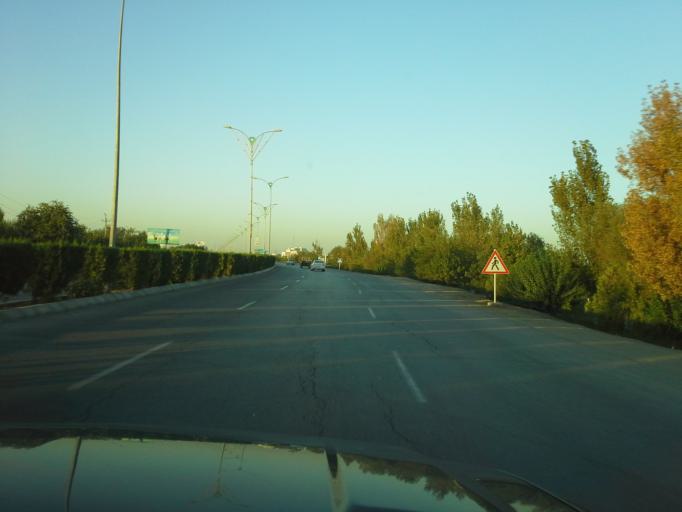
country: TM
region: Dasoguz
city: Dasoguz
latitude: 41.8110
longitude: 59.9121
